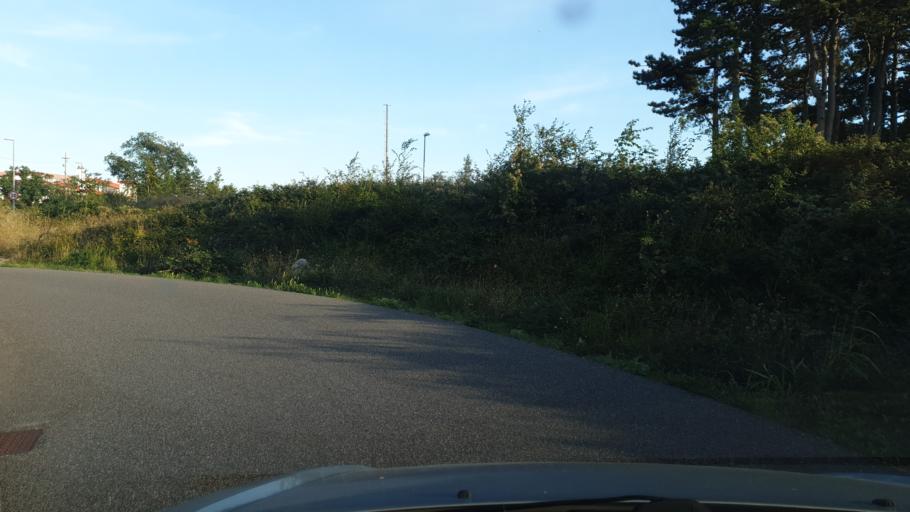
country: IT
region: Friuli Venezia Giulia
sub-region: Provincia di Trieste
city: Prosecco-Contovello
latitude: 45.7150
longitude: 13.7384
